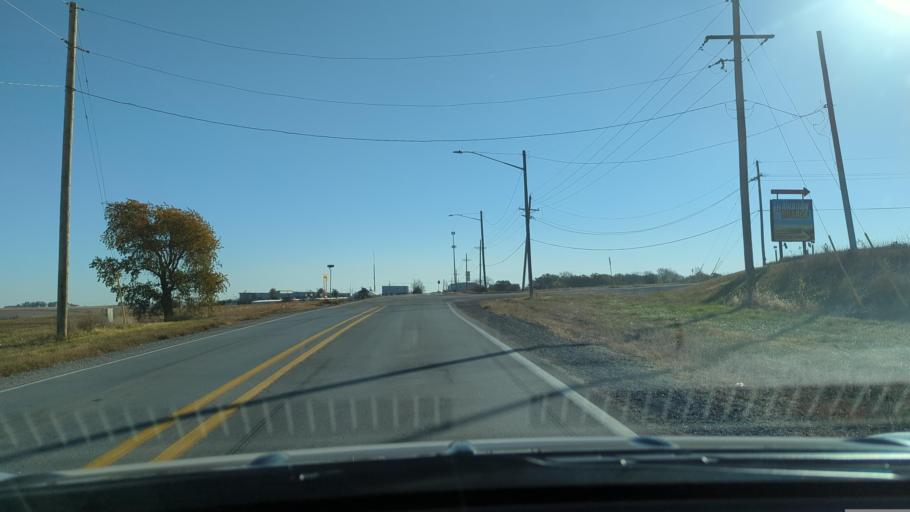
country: US
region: Nebraska
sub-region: Sarpy County
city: Papillion
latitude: 41.0890
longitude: -96.0486
